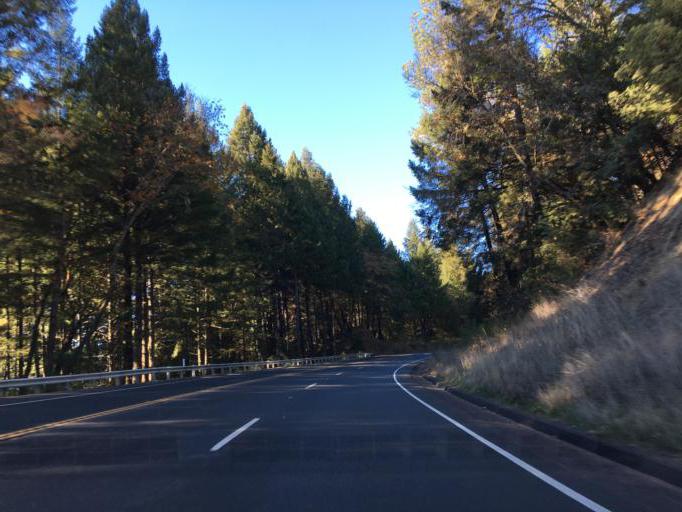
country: US
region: California
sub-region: Mendocino County
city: Brooktrails
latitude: 39.4664
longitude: -123.3533
